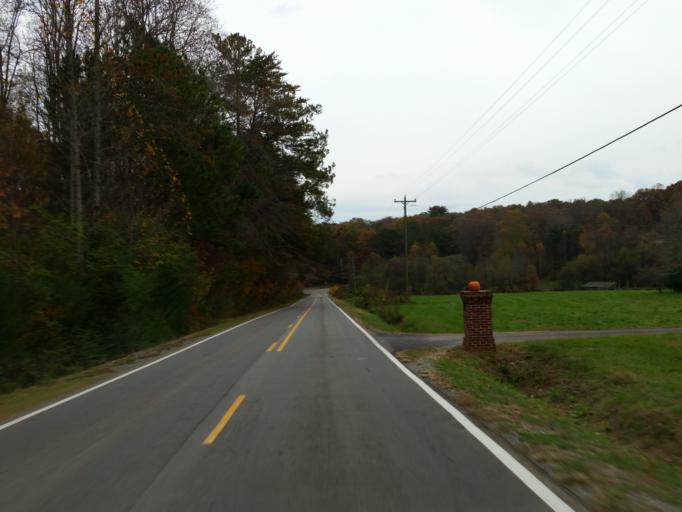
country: US
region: Georgia
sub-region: Gilmer County
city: Ellijay
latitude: 34.6439
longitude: -84.3380
